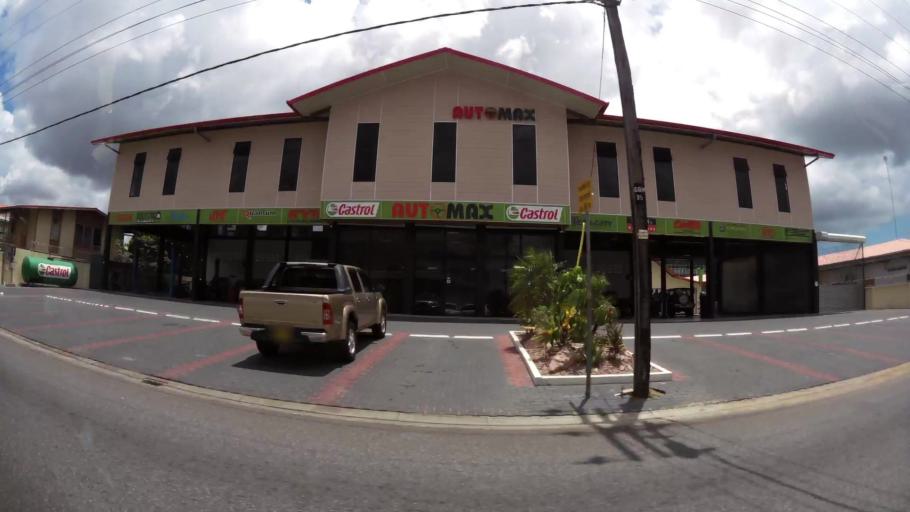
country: SR
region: Paramaribo
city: Paramaribo
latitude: 5.8535
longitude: -55.1373
